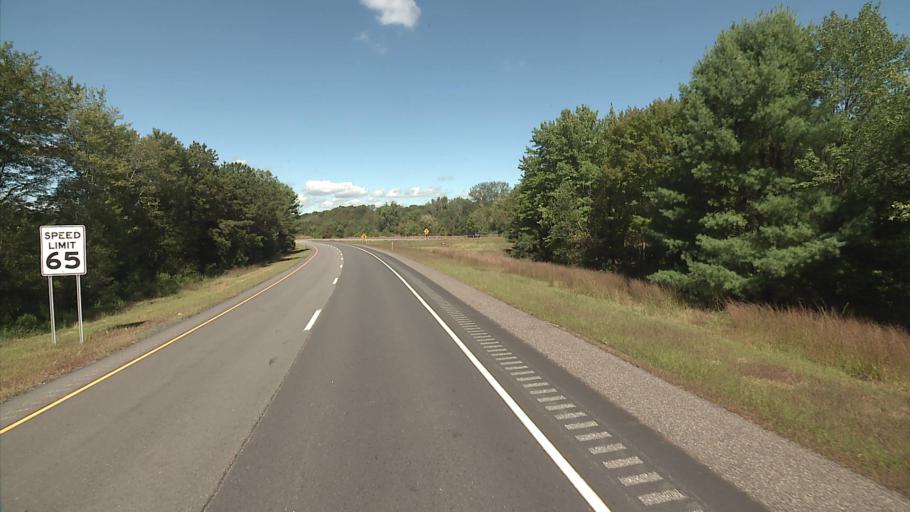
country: US
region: Connecticut
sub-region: New London County
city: Colchester
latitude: 41.5634
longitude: -72.3251
